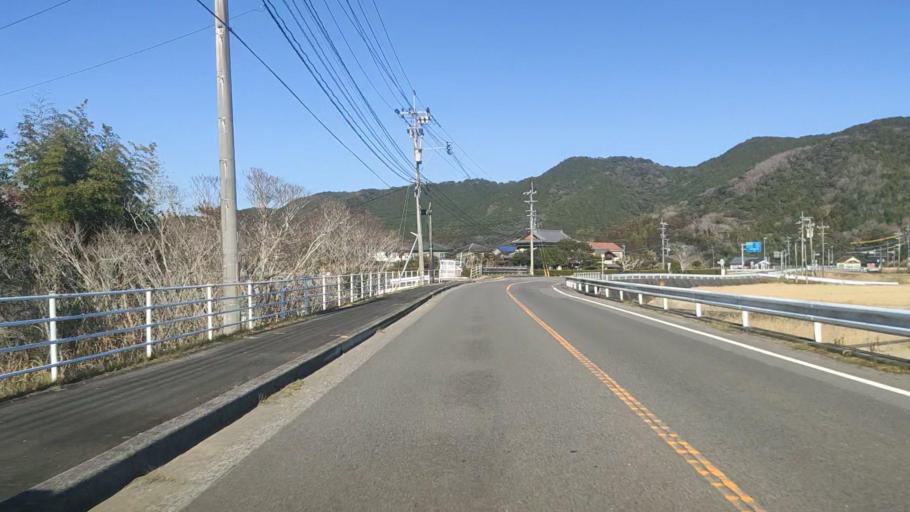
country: JP
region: Oita
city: Saiki
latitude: 32.9296
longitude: 131.9215
